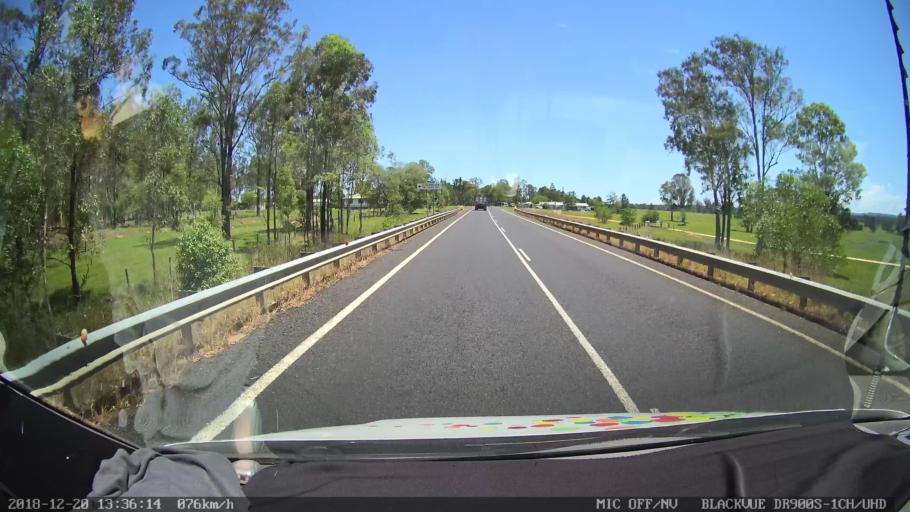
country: AU
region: New South Wales
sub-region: Clarence Valley
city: Maclean
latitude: -29.2797
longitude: 152.9904
